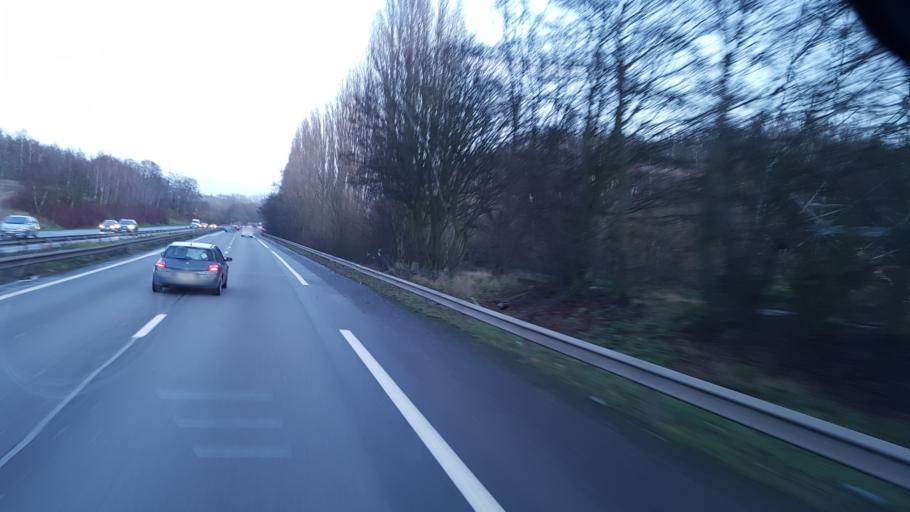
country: FR
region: Nord-Pas-de-Calais
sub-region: Departement du Pas-de-Calais
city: Billy-Montigny
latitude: 50.4315
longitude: 2.8922
